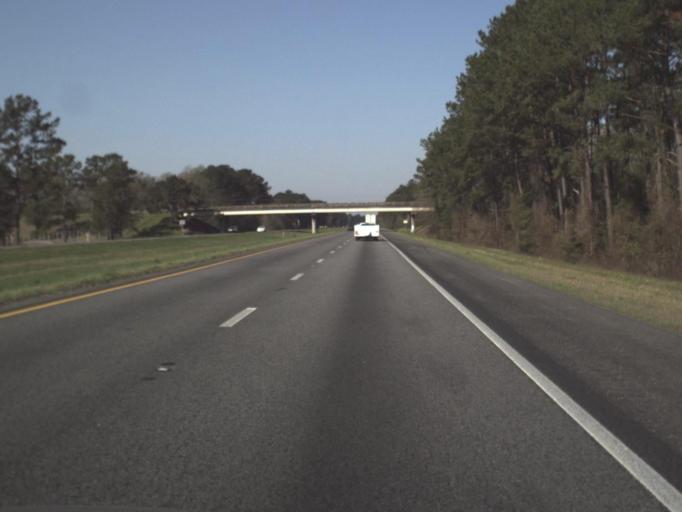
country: US
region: Florida
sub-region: Jefferson County
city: Monticello
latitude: 30.4786
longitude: -83.9179
